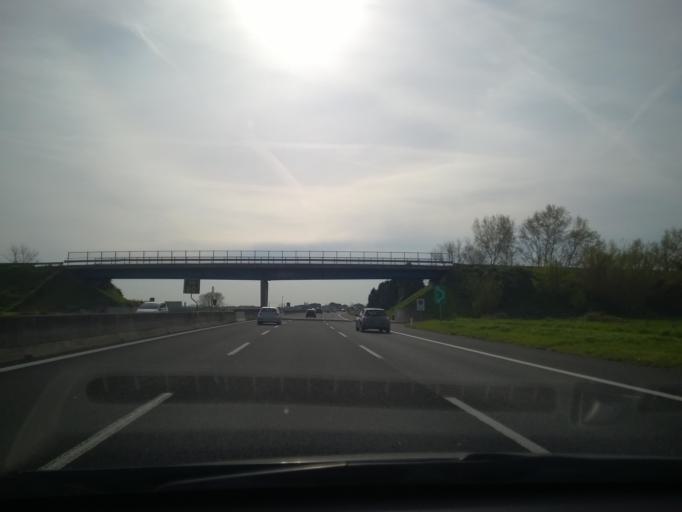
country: IT
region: Emilia-Romagna
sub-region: Forli-Cesena
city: Sala
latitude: 44.1333
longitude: 12.3695
